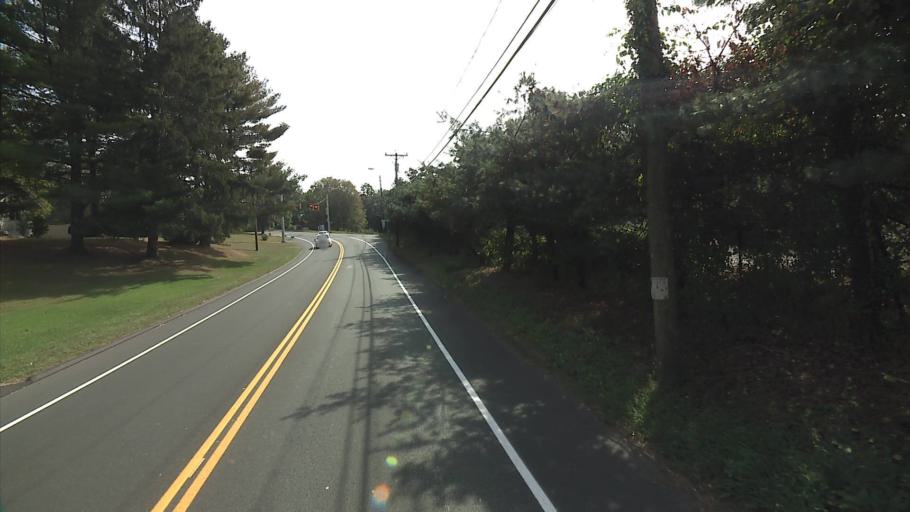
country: US
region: Connecticut
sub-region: Fairfield County
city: Newtown
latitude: 41.4084
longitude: -73.2649
